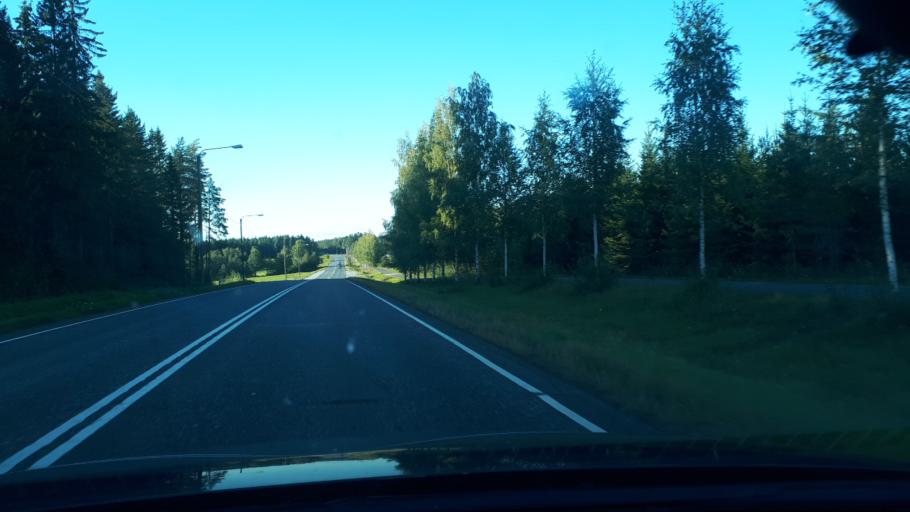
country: FI
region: Northern Savo
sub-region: Ylae-Savo
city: Lapinlahti
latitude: 63.4318
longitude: 27.3275
